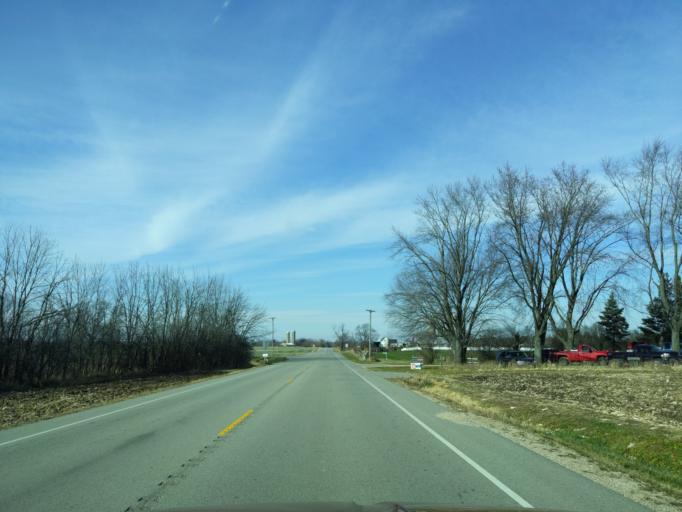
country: US
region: Wisconsin
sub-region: Walworth County
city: Elkhorn
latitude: 42.6980
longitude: -88.5690
